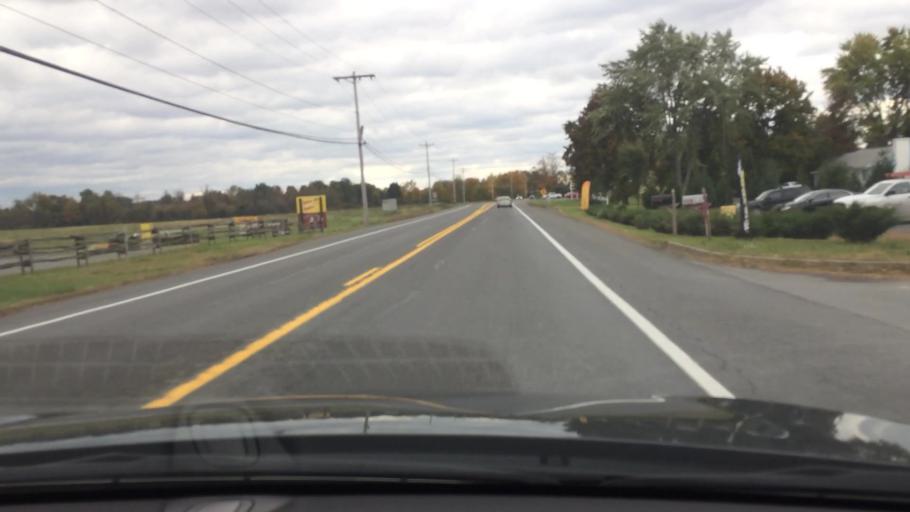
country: US
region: New York
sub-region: Columbia County
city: Valatie
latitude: 42.4350
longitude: -73.6871
